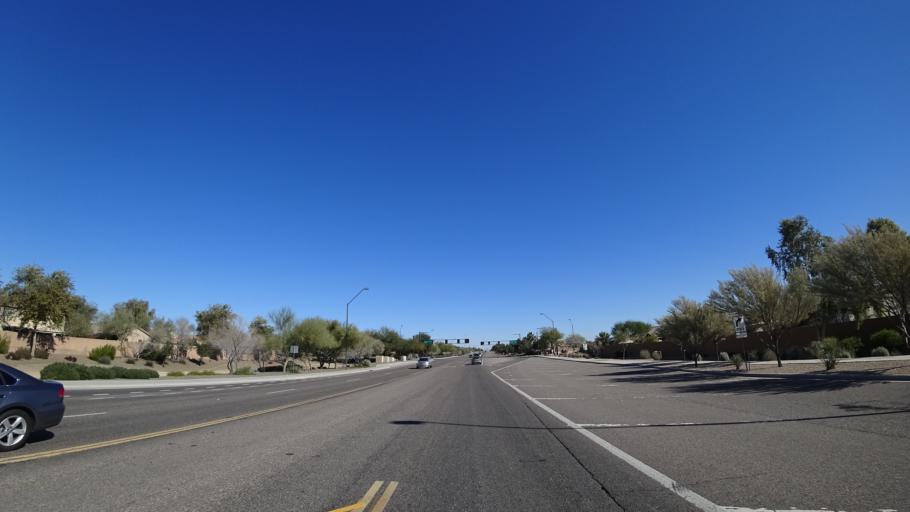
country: US
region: Arizona
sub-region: Maricopa County
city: Goodyear
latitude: 33.4356
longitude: -112.4198
